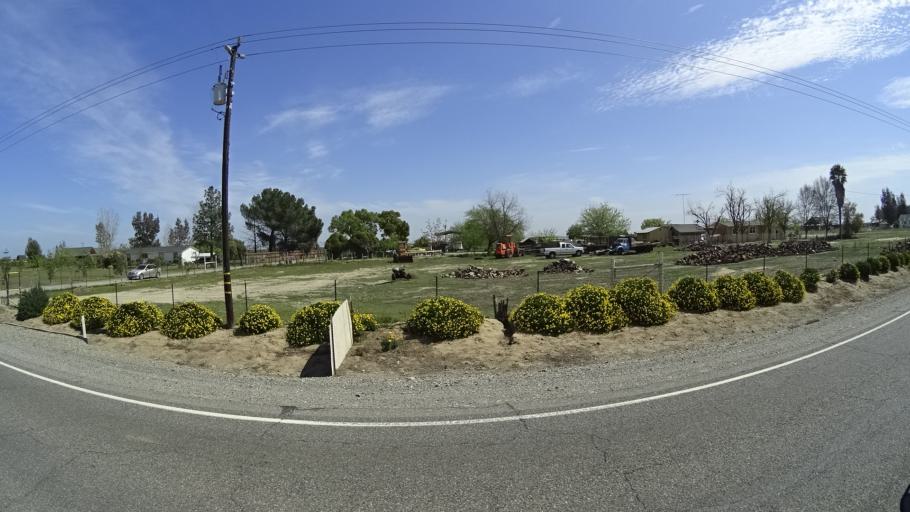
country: US
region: California
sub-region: Glenn County
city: Willows
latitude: 39.6334
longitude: -122.1974
